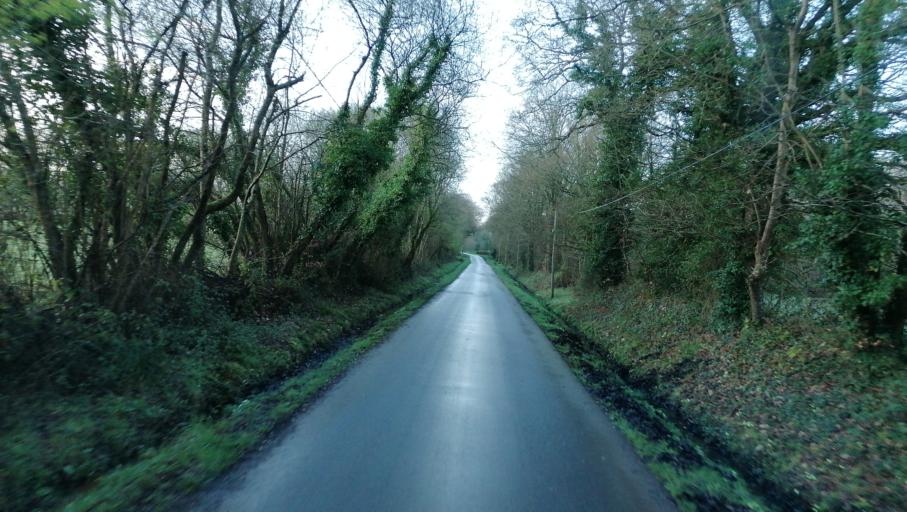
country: FR
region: Brittany
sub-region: Departement des Cotes-d'Armor
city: Plouha
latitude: 48.6615
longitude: -2.9473
